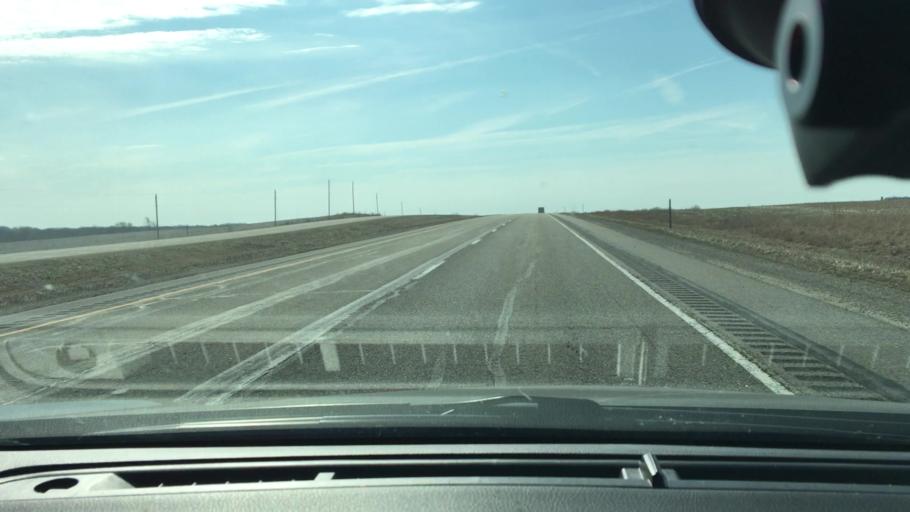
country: US
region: Iowa
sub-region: Chickasaw County
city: Nashua
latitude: 42.9893
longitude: -92.5912
